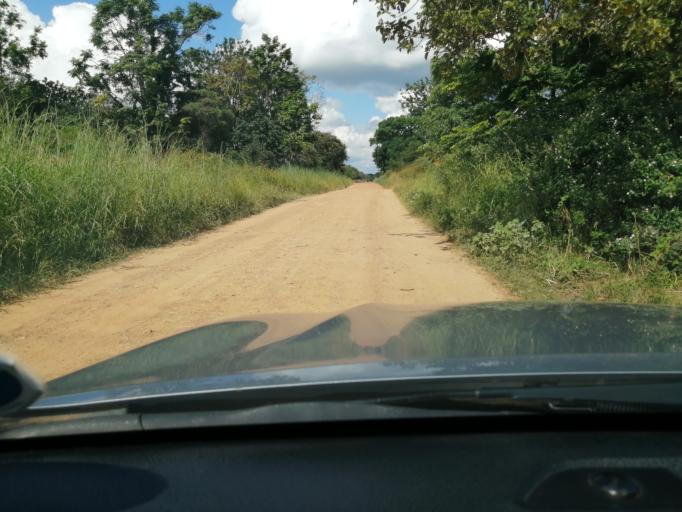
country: ZM
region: Lusaka
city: Lusaka
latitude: -15.2026
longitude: 28.0580
